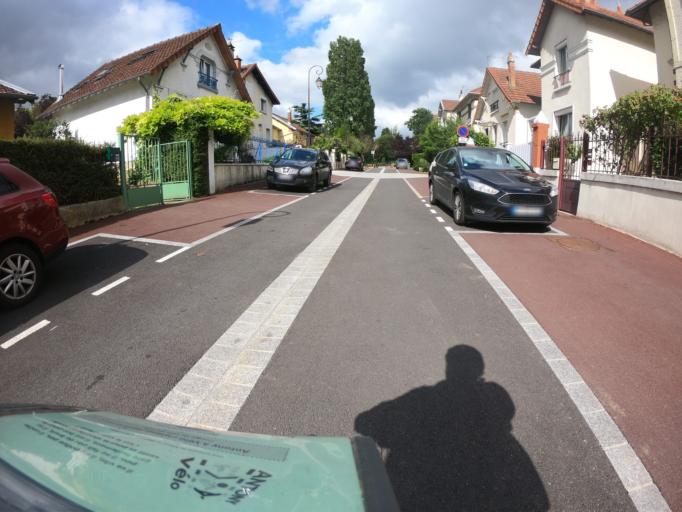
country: FR
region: Ile-de-France
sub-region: Departement des Hauts-de-Seine
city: Antony
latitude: 48.7602
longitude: 2.2933
